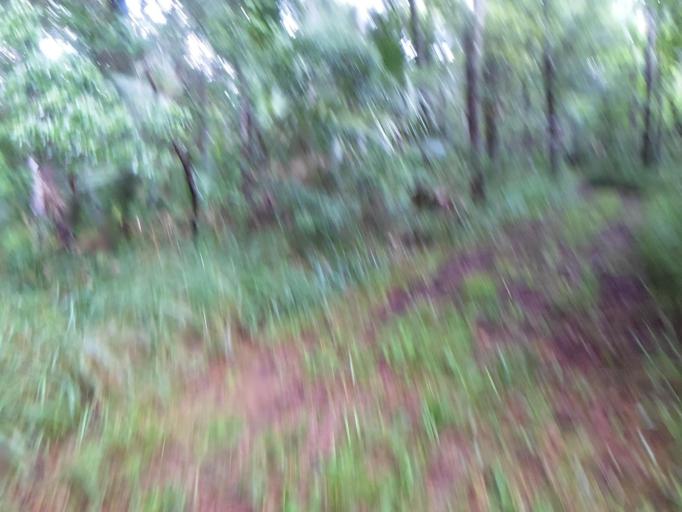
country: US
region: Florida
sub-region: Putnam County
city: Palatka
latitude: 29.6762
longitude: -81.7542
